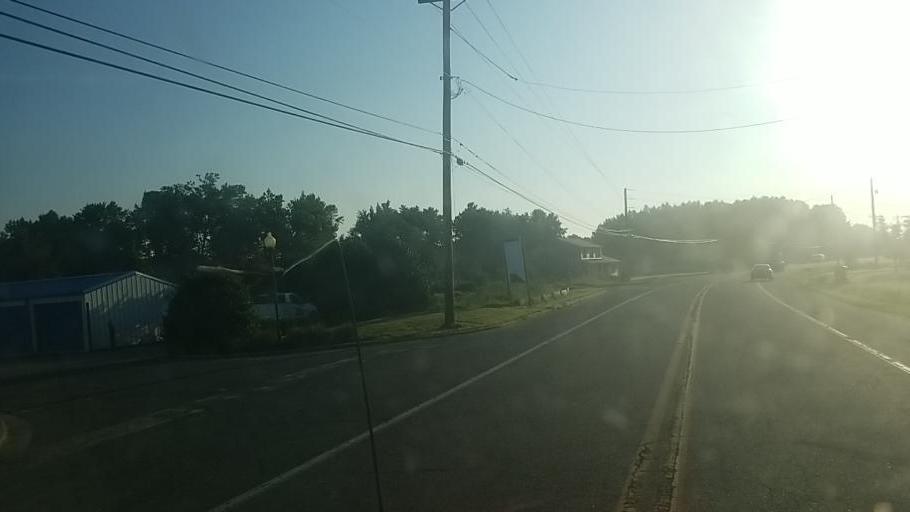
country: US
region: Delaware
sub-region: Sussex County
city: Selbyville
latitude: 38.4620
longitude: -75.1904
